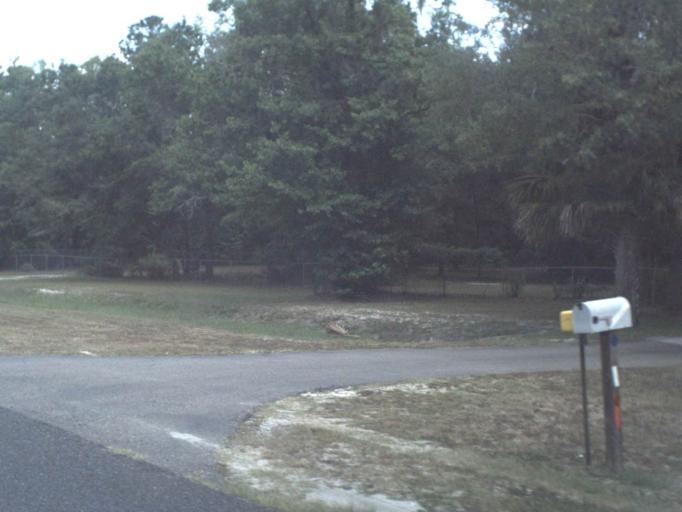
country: US
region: Florida
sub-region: Alachua County
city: Hawthorne
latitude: 29.5992
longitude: -82.1273
